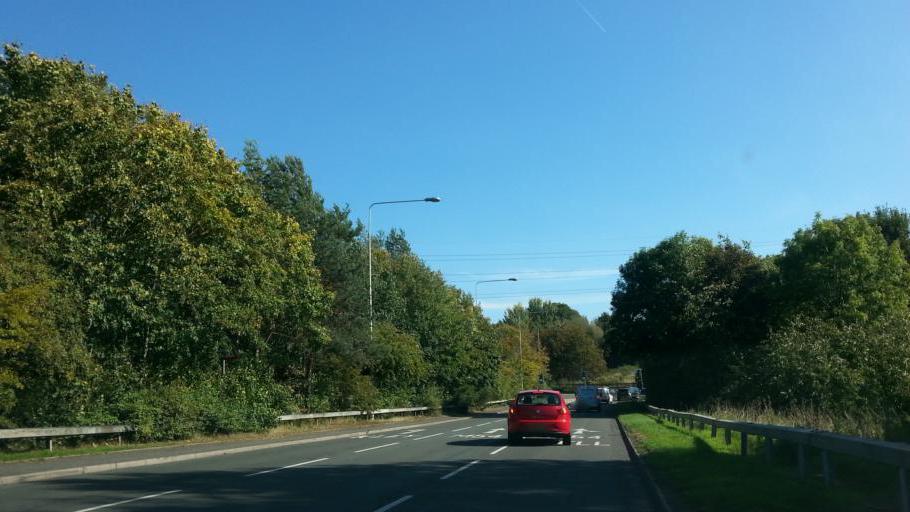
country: GB
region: England
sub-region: Shropshire
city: Hadley
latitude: 52.6966
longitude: -2.4920
